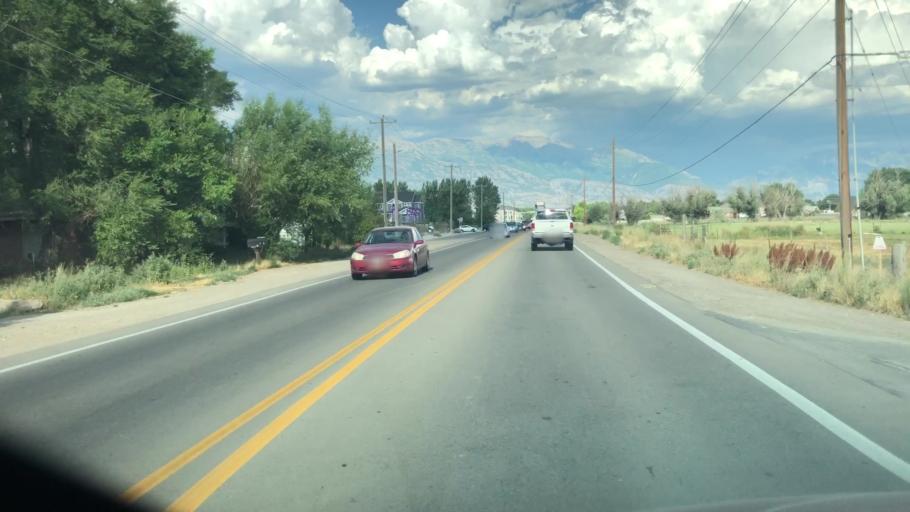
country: US
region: Utah
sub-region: Utah County
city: Saratoga Springs
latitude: 40.3873
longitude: -111.8918
